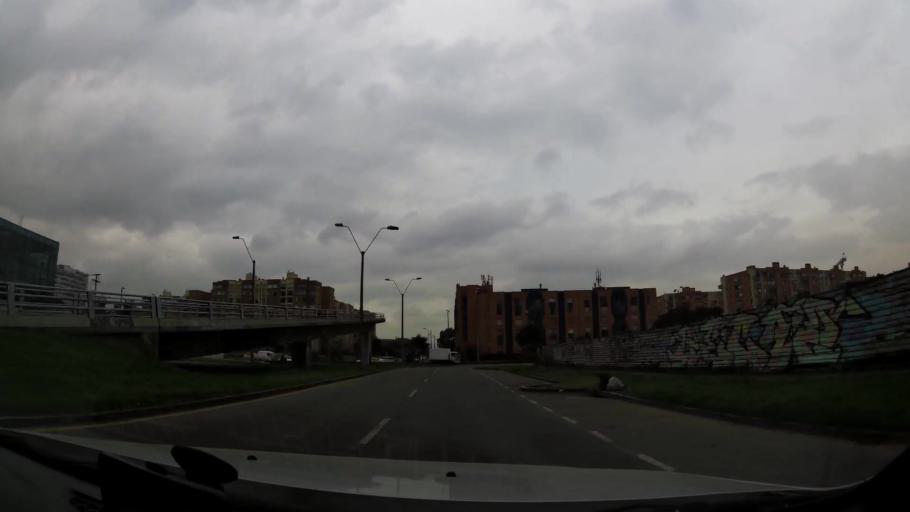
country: CO
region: Bogota D.C.
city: Bogota
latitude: 4.6517
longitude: -74.1073
